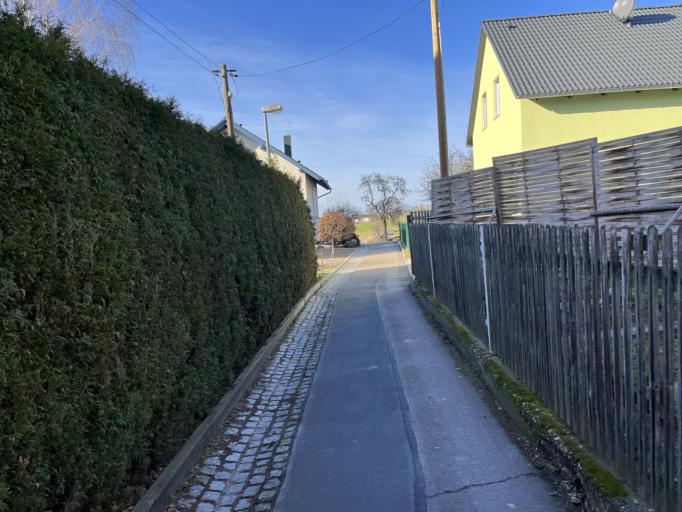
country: DE
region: Saxony
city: Tharandt
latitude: 51.0178
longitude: 13.5687
